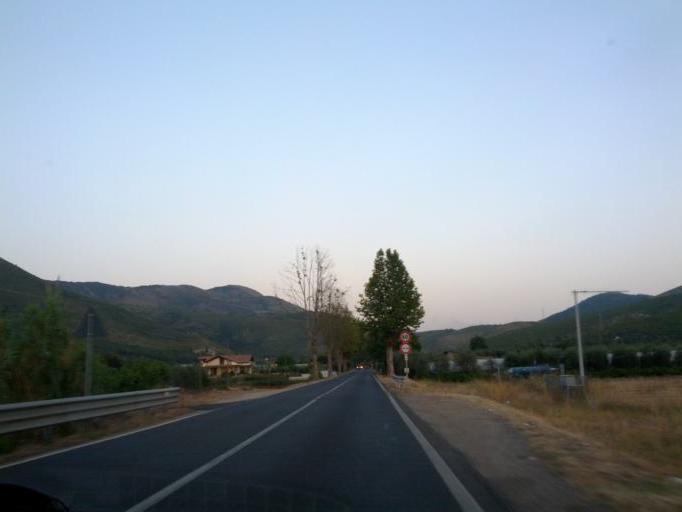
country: IT
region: Latium
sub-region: Provincia di Latina
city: Fondi
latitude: 41.3329
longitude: 13.4636
